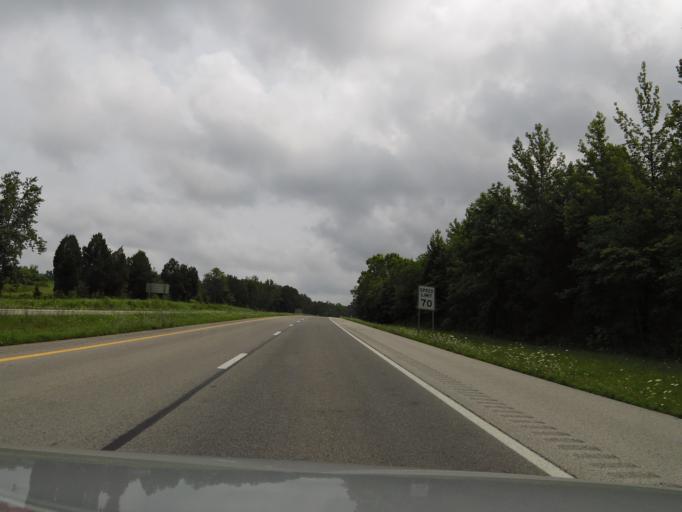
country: US
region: Kentucky
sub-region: Ohio County
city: Oak Grove
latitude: 37.3897
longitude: -86.7984
